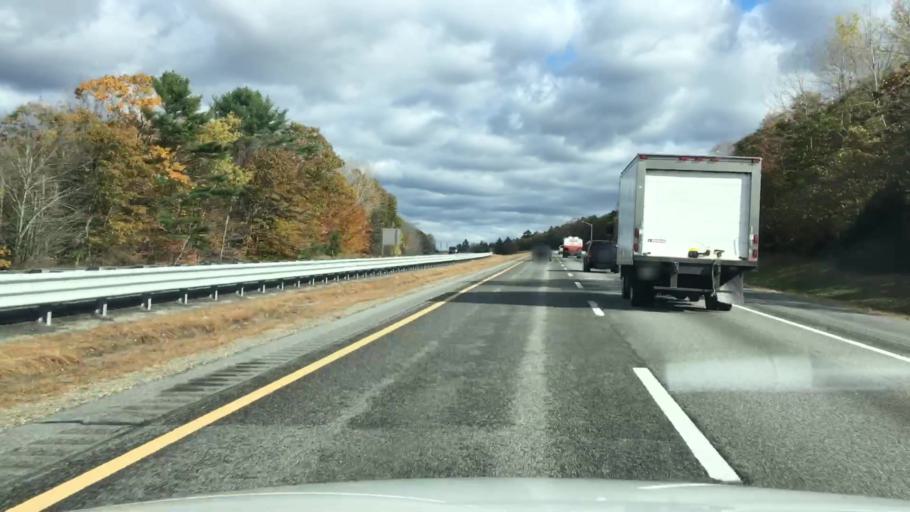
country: US
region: Maine
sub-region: Sagadahoc County
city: Topsham
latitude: 43.9182
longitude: -70.0184
